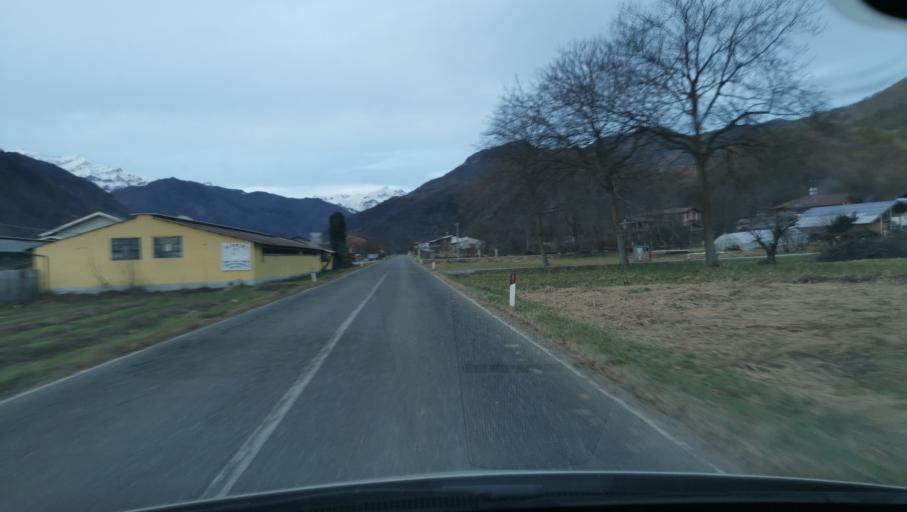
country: IT
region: Piedmont
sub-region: Provincia di Cuneo
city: Valgrana
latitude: 44.4125
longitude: 7.3603
